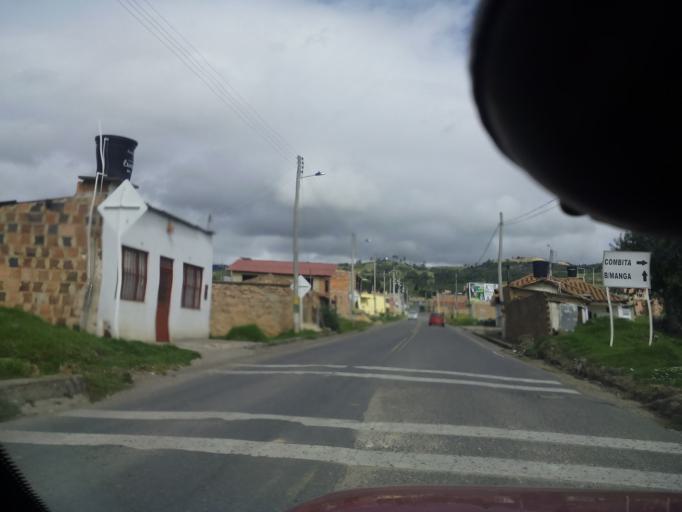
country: CO
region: Boyaca
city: Combita
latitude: 5.6328
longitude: -73.3216
